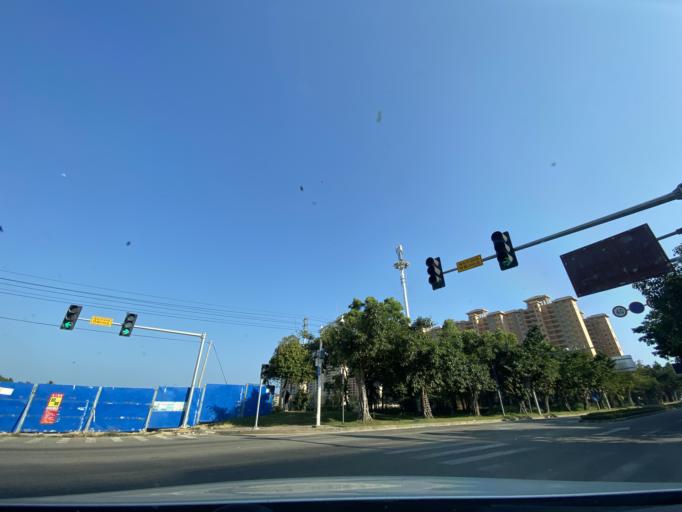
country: CN
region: Hainan
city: Xincun
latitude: 18.4235
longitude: 109.9610
